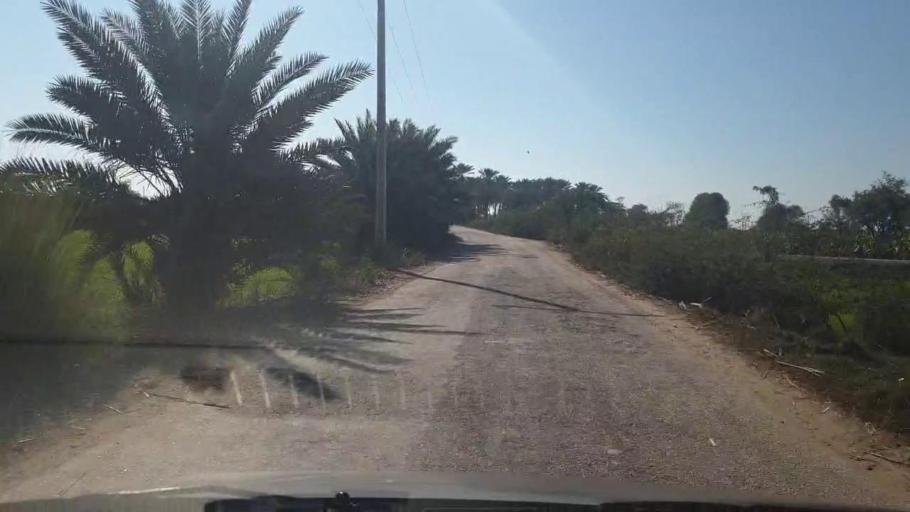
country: PK
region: Sindh
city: Bozdar
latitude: 27.2498
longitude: 68.6519
